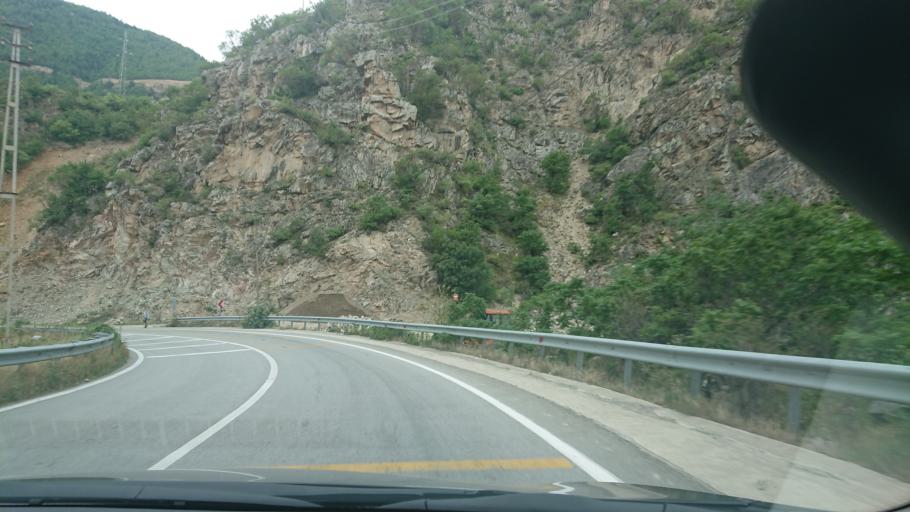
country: TR
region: Gumushane
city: Kurtun
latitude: 40.7048
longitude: 39.0780
